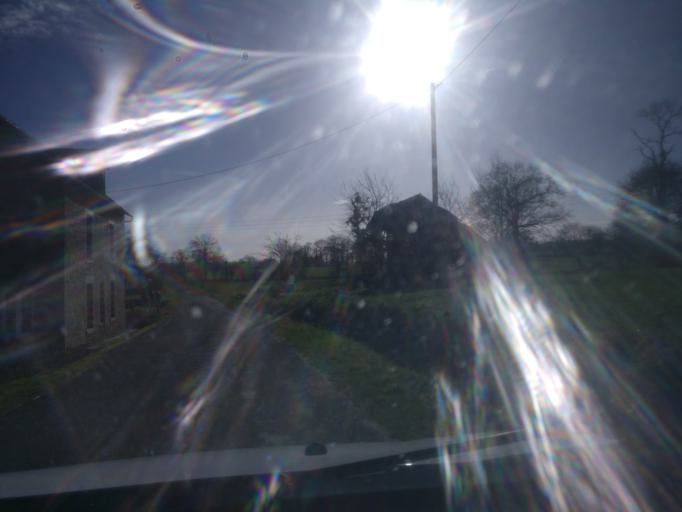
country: FR
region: Lower Normandy
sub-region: Departement de la Manche
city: Pontorson
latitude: 48.5189
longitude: -1.5187
